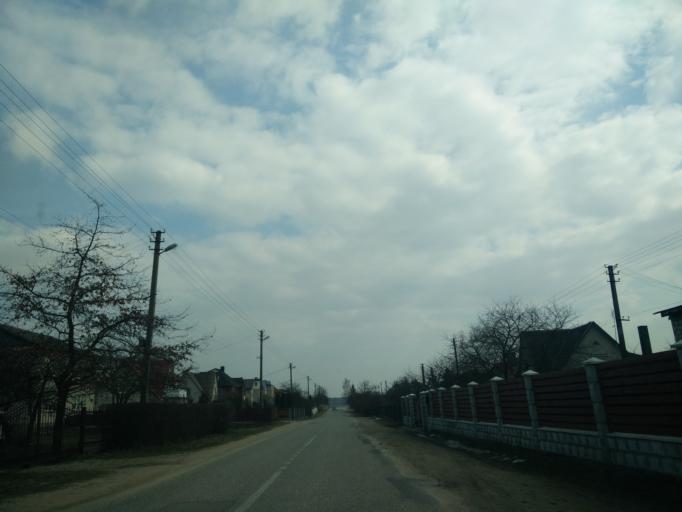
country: LT
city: Trakai
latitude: 54.6108
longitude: 24.9839
